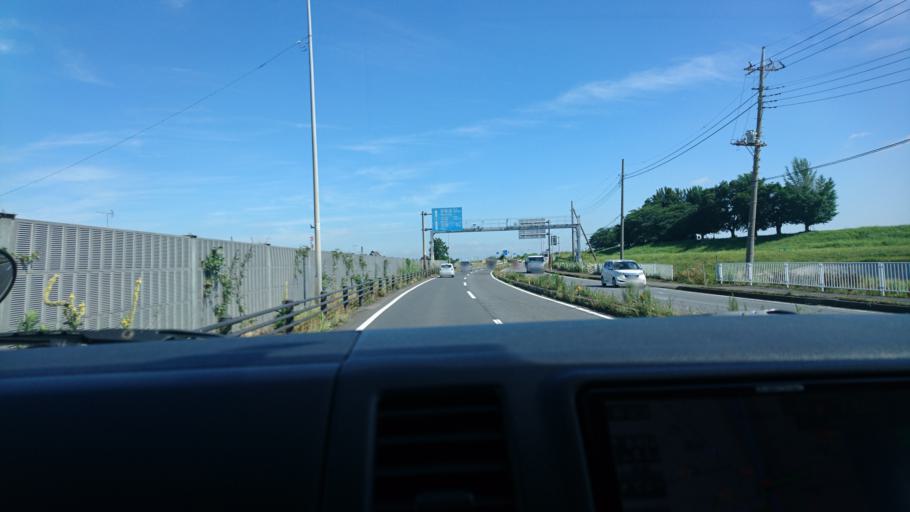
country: JP
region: Saitama
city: Kurihashi
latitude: 36.1353
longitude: 139.7063
